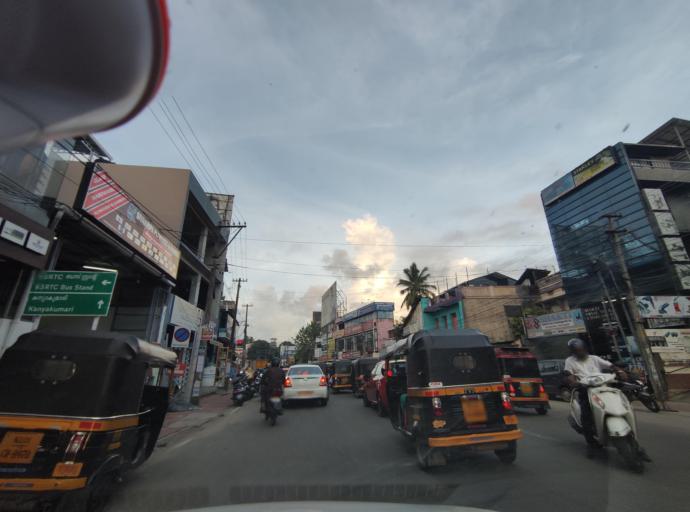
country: IN
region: Kerala
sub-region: Thiruvananthapuram
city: Thiruvananthapuram
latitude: 8.4845
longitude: 76.9541
